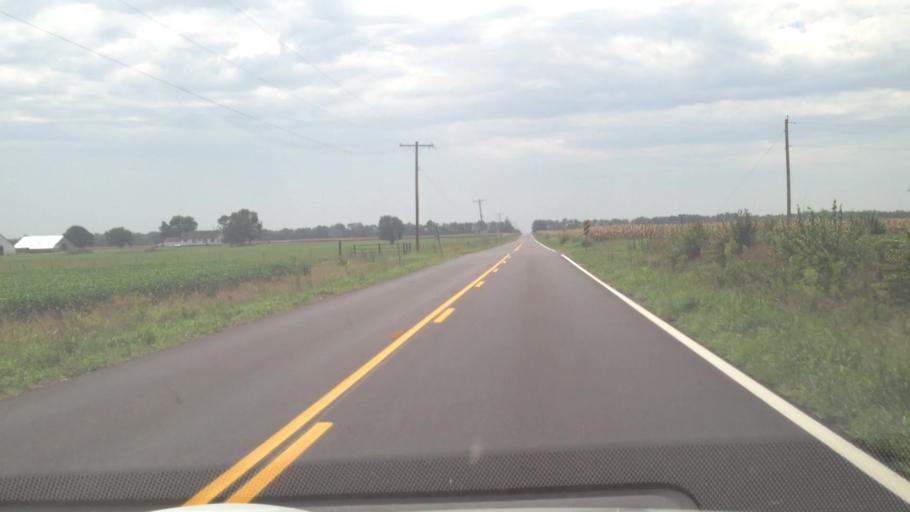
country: US
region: Kansas
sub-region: Crawford County
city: Girard
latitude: 37.6463
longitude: -94.9698
